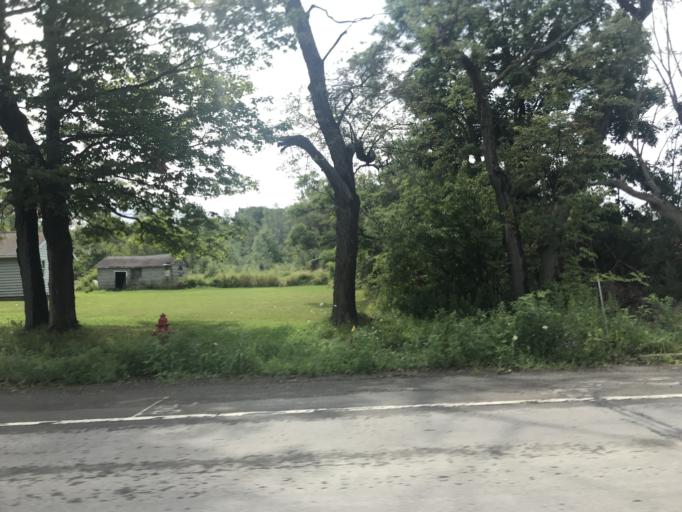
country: US
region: New York
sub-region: Chautauqua County
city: Silver Creek
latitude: 42.5455
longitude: -79.1857
